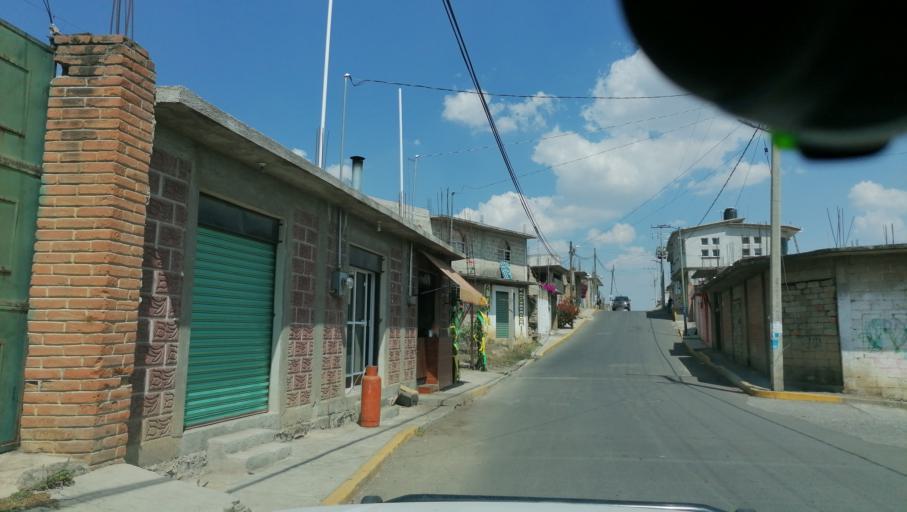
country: MX
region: Puebla
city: San Andres Calpan
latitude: 19.1039
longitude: -98.4809
